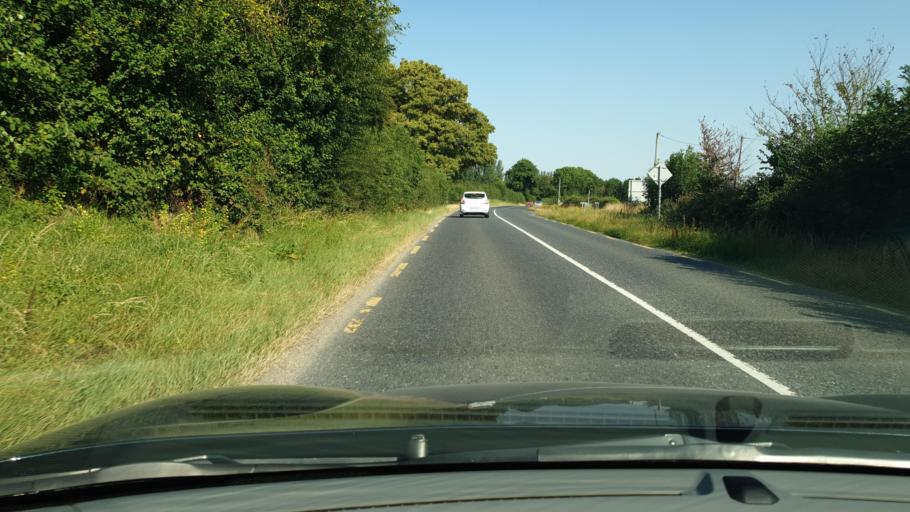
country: IE
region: Leinster
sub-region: An Mhi
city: Navan
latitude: 53.6466
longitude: -6.6441
